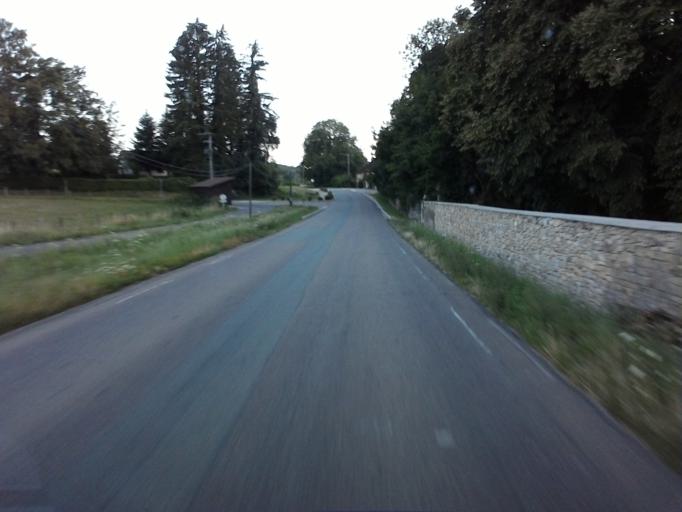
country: FR
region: Franche-Comte
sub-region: Departement du Jura
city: Salins-les-Bains
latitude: 47.0131
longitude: 5.8554
